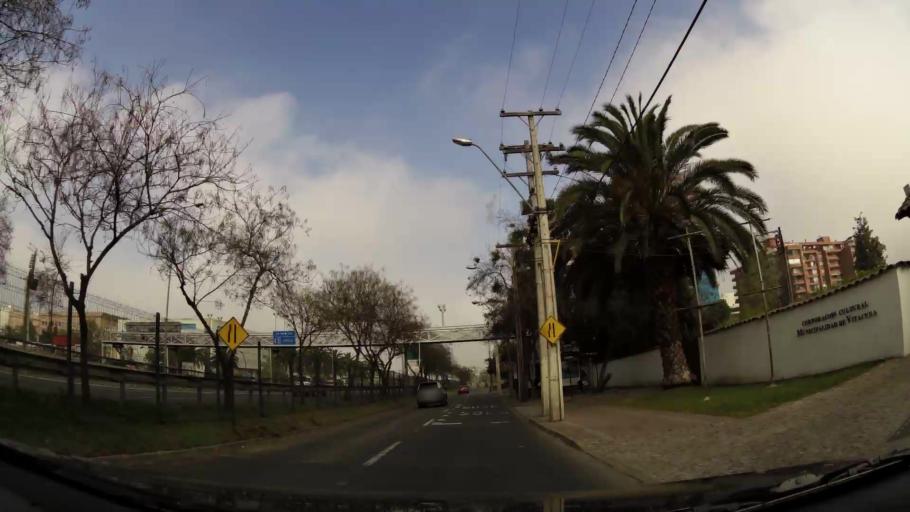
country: CL
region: Santiago Metropolitan
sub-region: Provincia de Santiago
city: Villa Presidente Frei, Nunoa, Santiago, Chile
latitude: -33.3882
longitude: -70.5446
